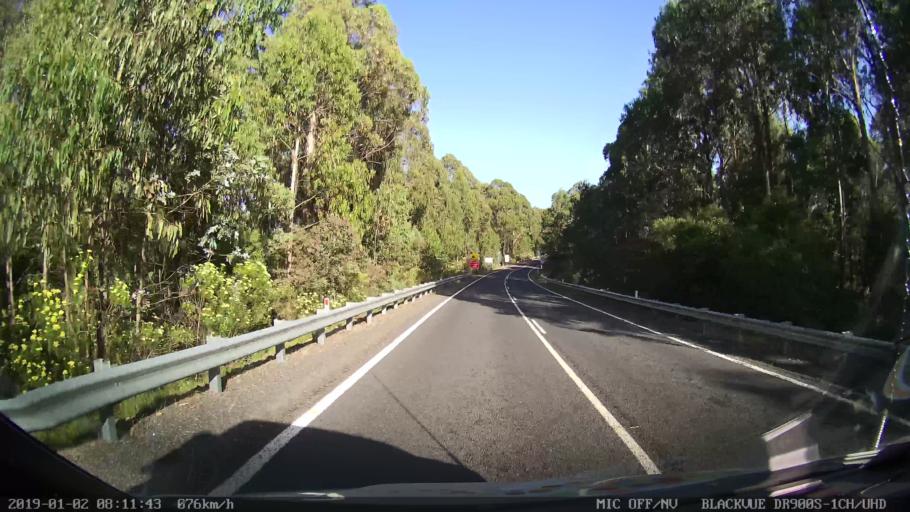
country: AU
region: New South Wales
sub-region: Tumut Shire
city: Tumut
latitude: -35.5940
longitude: 148.3543
